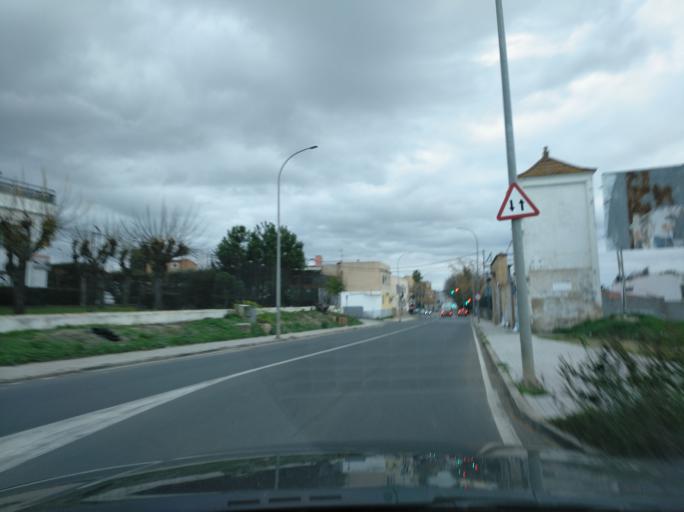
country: ES
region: Extremadura
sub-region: Provincia de Badajoz
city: Badajoz
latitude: 38.8942
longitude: -6.9825
